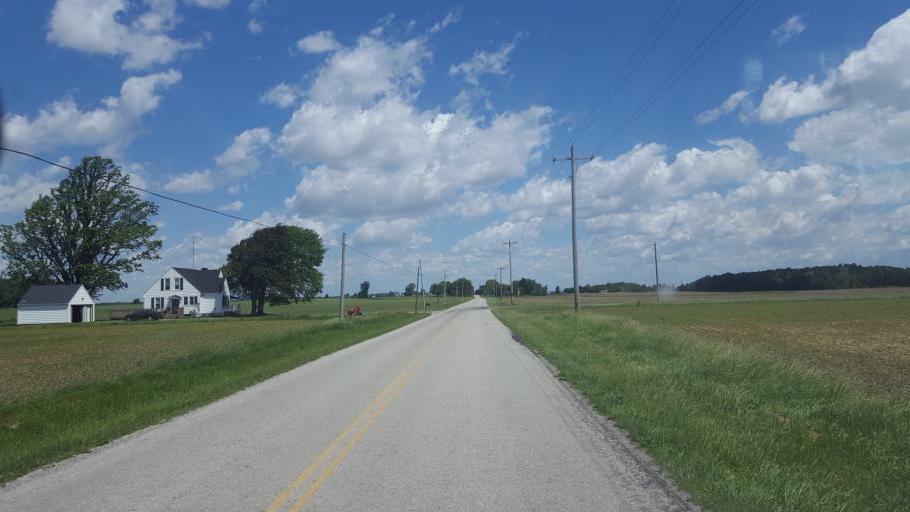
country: US
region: Ohio
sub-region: Richland County
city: Shelby
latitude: 40.8570
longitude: -82.7198
